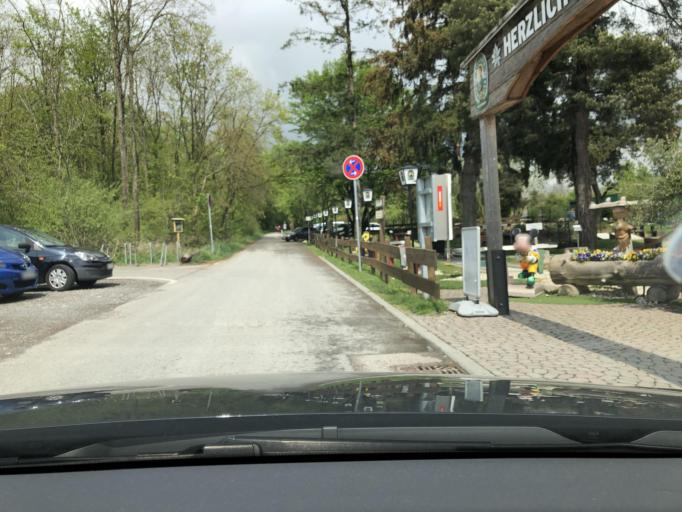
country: DE
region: Baden-Wuerttemberg
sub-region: Regierungsbezirk Stuttgart
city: Rutesheim
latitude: 48.8125
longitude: 8.9235
